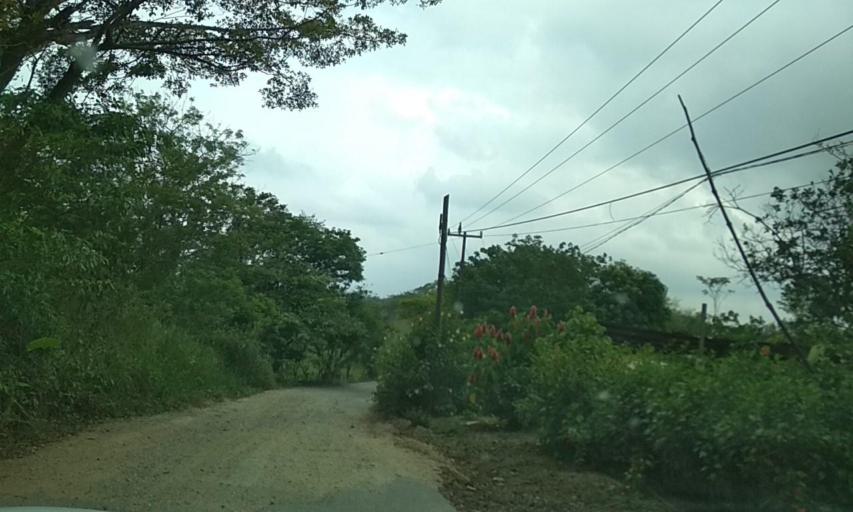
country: MX
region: Veracruz
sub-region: Uxpanapa
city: Poblado 10
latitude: 17.5033
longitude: -94.1570
